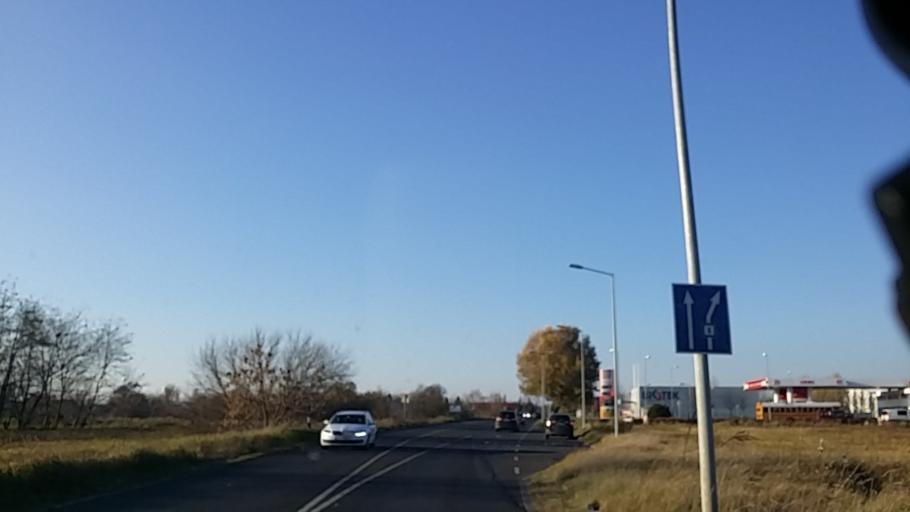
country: HU
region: Budapest
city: Budapest XVII. keruelet
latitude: 47.5004
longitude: 19.2171
